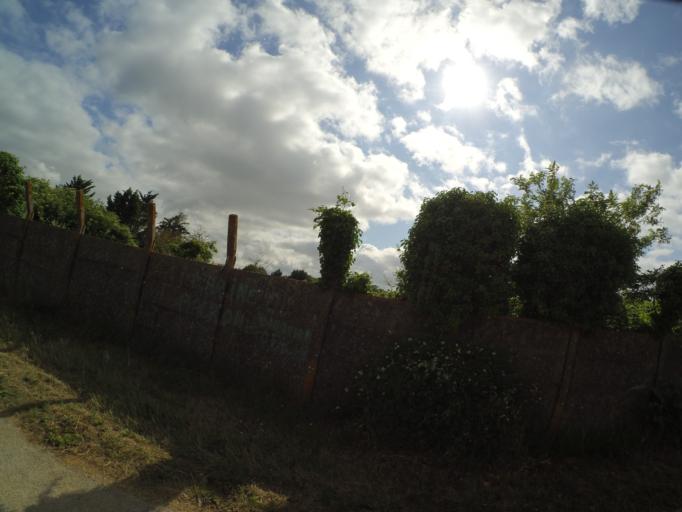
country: FR
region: Poitou-Charentes
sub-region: Departement de la Charente-Maritime
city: Angoulins
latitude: 46.1092
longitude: -1.1174
